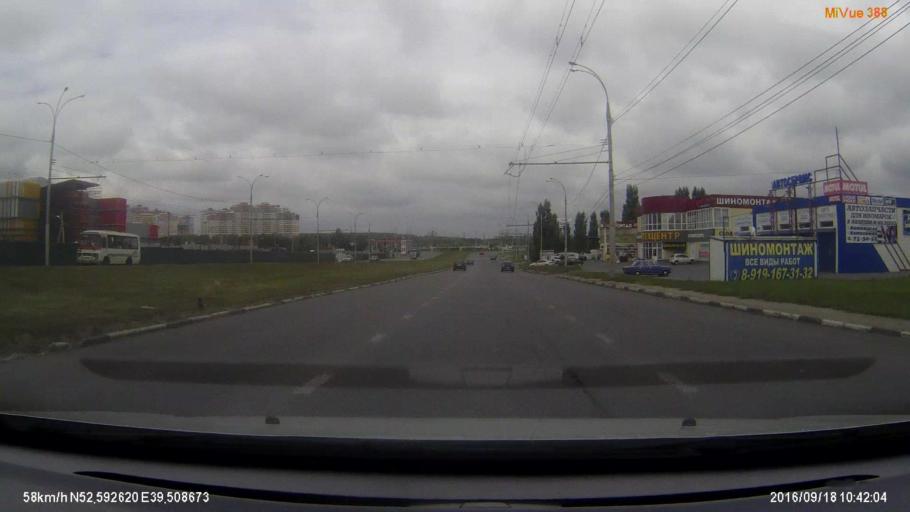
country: RU
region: Lipetsk
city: Syrskoye
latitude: 52.5925
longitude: 39.5089
